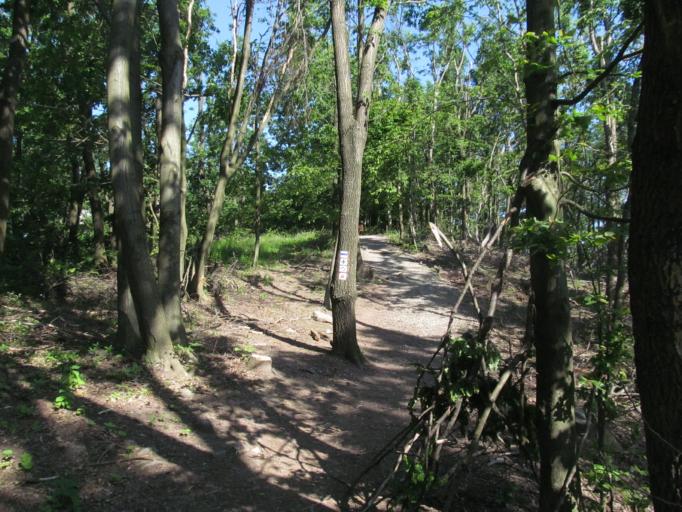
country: HU
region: Pest
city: Pilisszentkereszt
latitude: 47.7191
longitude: 18.9029
